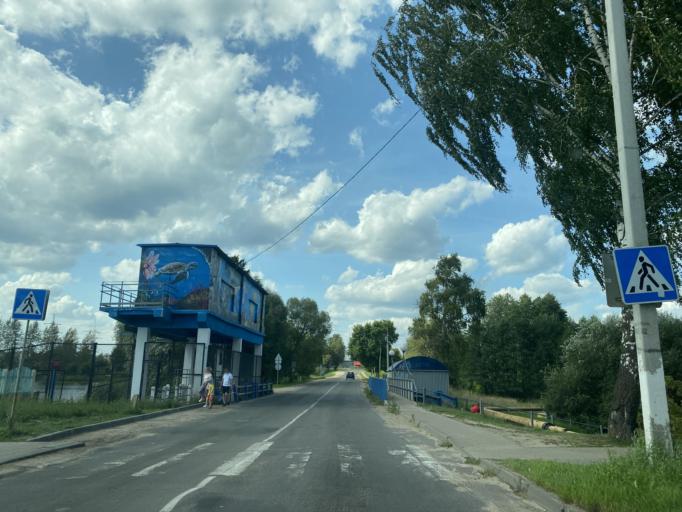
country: BY
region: Minsk
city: Horad Zhodzina
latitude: 54.0996
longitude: 28.3514
